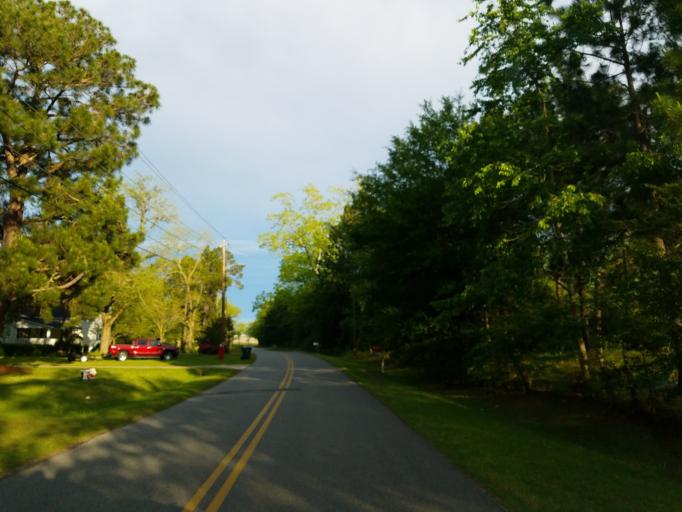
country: US
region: Georgia
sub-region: Turner County
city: Ashburn
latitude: 31.6941
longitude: -83.6439
